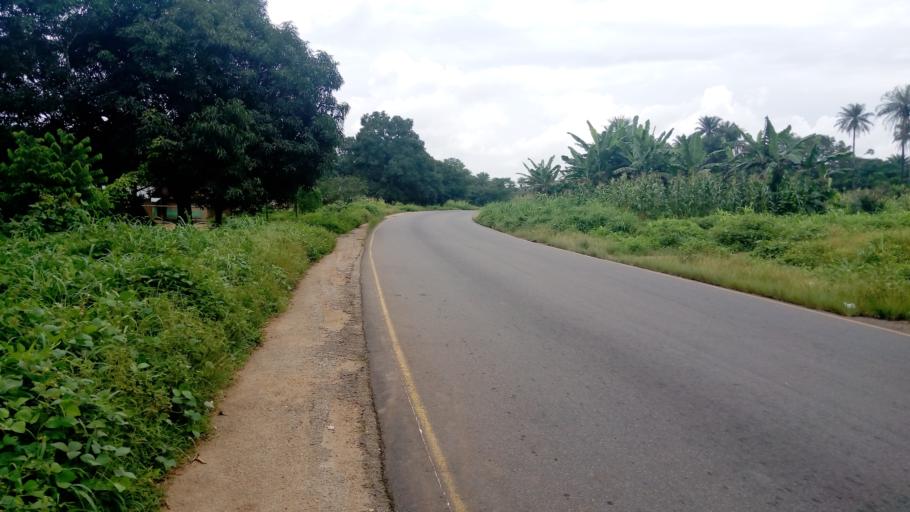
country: SL
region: Northern Province
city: Port Loko
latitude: 8.5069
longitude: -12.7611
